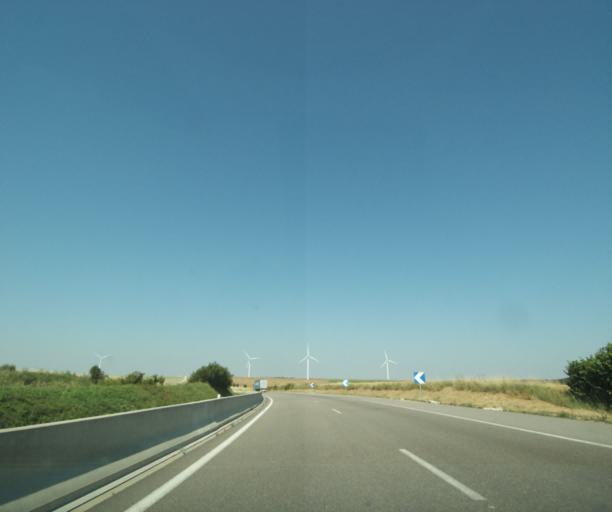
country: FR
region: Lorraine
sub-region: Departement de la Meuse
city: Ligny-en-Barrois
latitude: 48.7047
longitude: 5.4340
